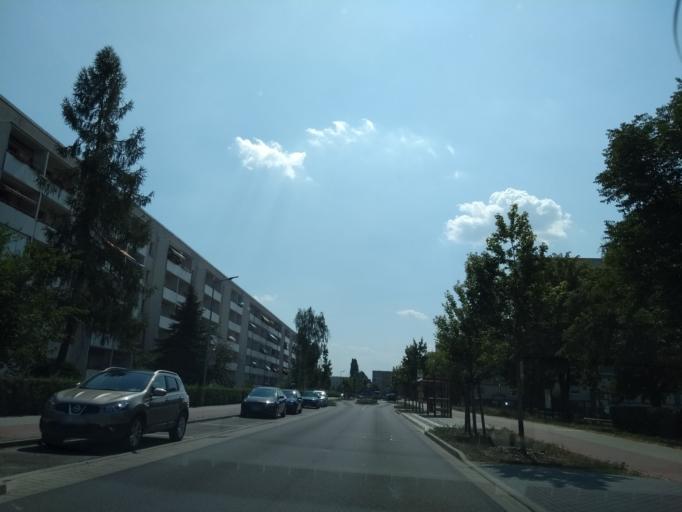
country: DE
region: Brandenburg
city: Lubbenau
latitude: 51.8625
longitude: 13.9413
